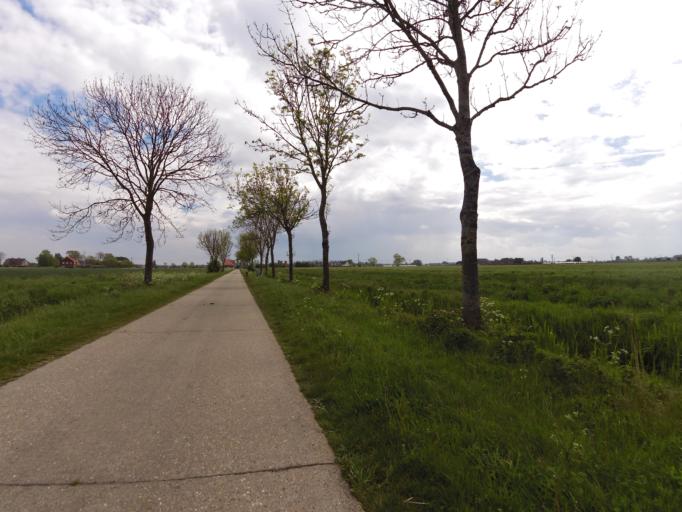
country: BE
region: Flanders
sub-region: Provincie West-Vlaanderen
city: Koekelare
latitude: 51.1077
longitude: 2.9179
